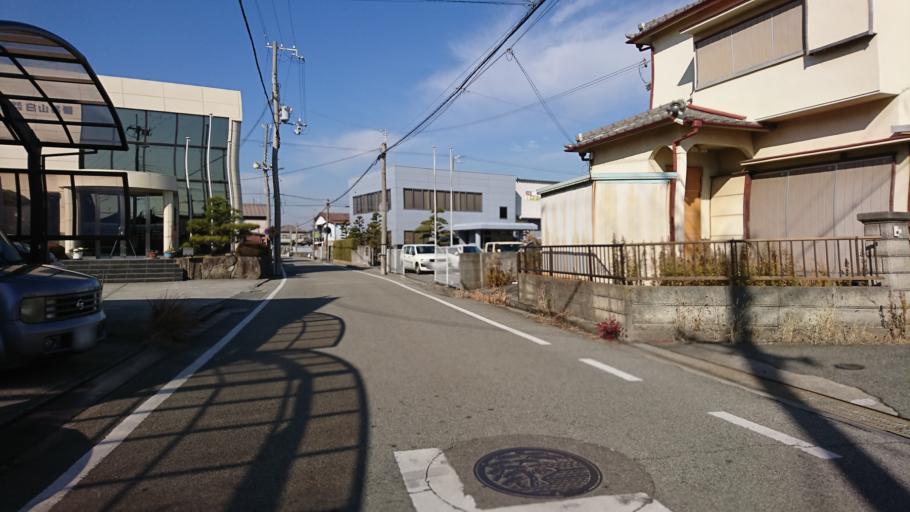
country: JP
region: Hyogo
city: Kakogawacho-honmachi
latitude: 34.7505
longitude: 134.7973
